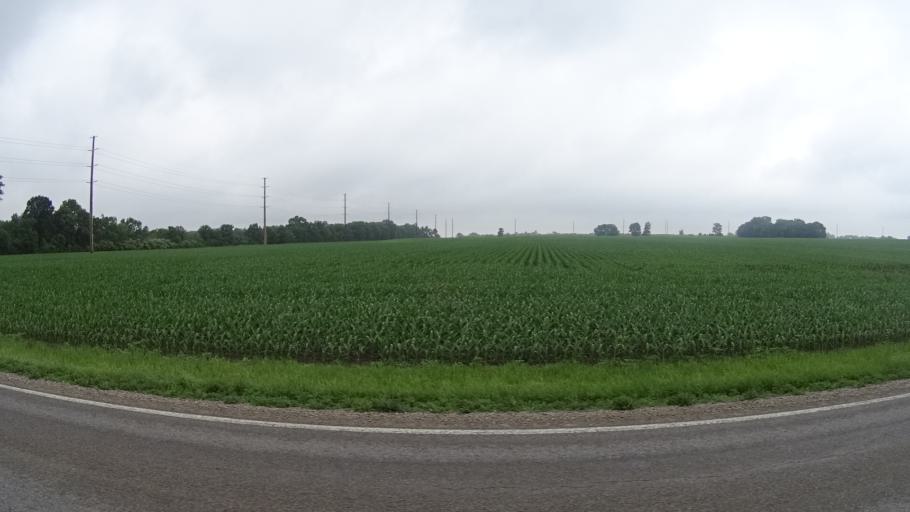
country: US
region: Ohio
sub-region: Huron County
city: Bellevue
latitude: 41.3466
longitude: -82.7673
